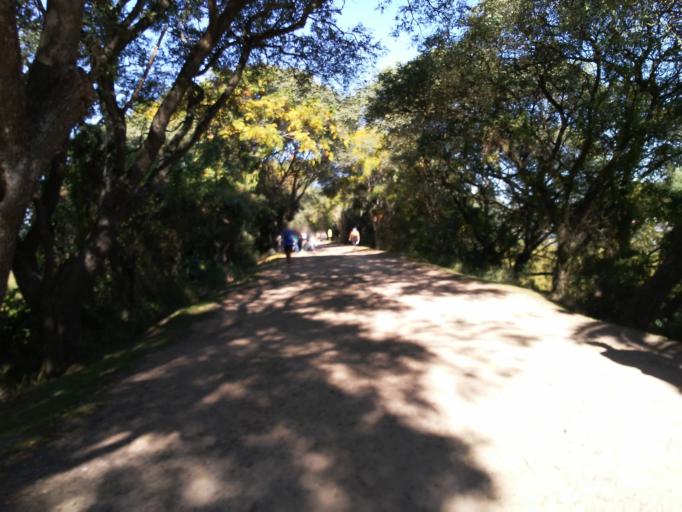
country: AR
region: Buenos Aires F.D.
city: Buenos Aires
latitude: -34.6131
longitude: -58.3561
